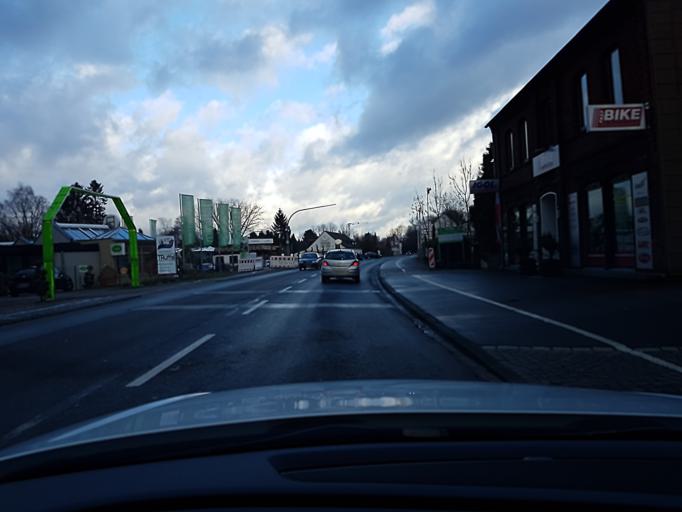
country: DE
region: North Rhine-Westphalia
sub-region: Regierungsbezirk Dusseldorf
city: Muelheim (Ruhr)
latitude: 51.3893
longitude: 6.8669
